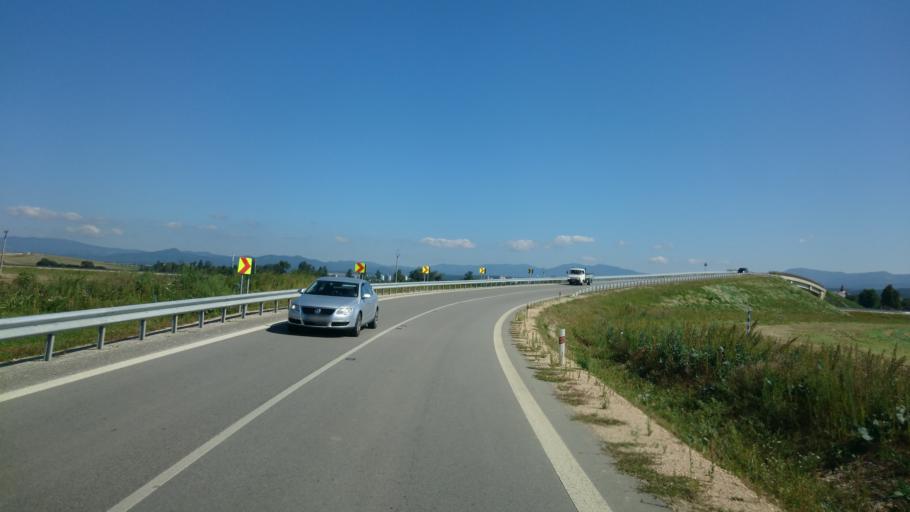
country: SK
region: Nitriansky
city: Banovce nad Bebravou
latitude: 48.7053
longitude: 18.2314
